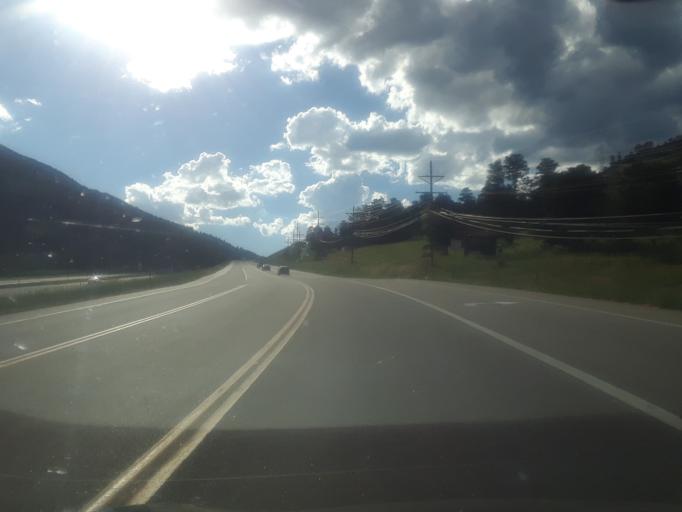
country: US
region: Colorado
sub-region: Clear Creek County
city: Idaho Springs
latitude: 39.7198
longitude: -105.4021
